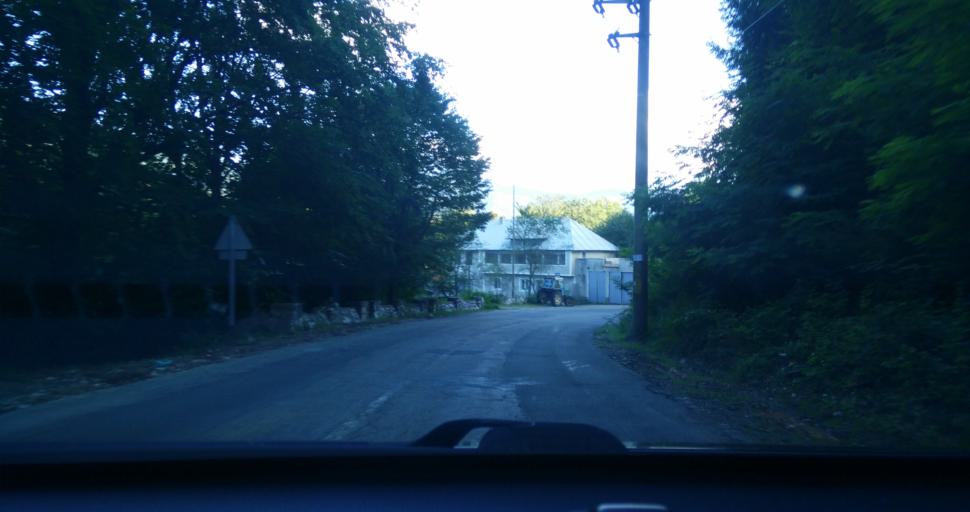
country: RO
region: Bihor
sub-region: Oras Nucet
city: Nucet
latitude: 46.5045
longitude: 22.6159
